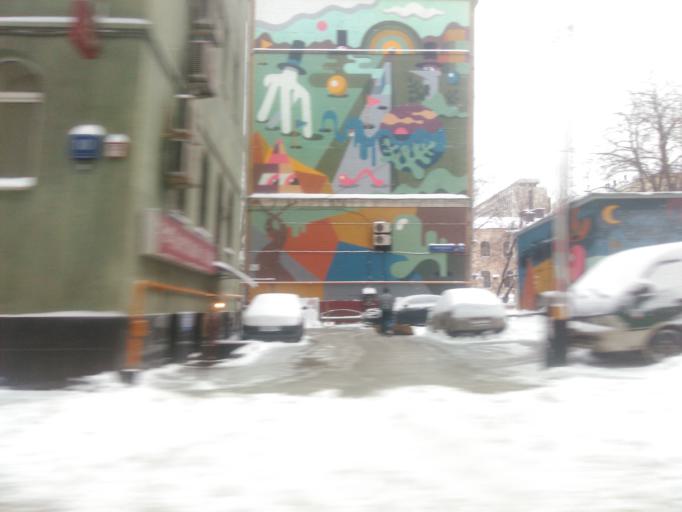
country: RU
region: Moscow
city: Mar'ina Roshcha
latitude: 55.7770
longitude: 37.6306
